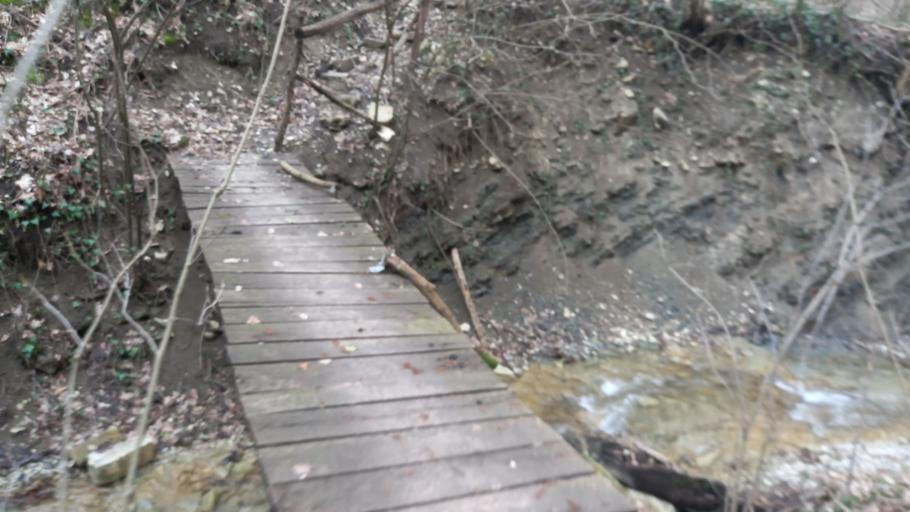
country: RU
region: Krasnodarskiy
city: Pshada
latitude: 44.5123
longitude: 38.4022
